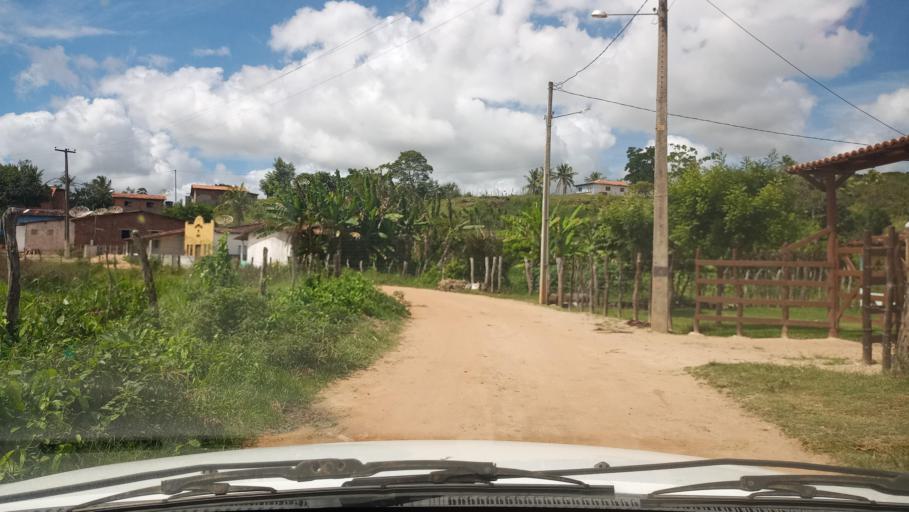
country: BR
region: Rio Grande do Norte
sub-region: Goianinha
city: Goianinha
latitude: -6.2621
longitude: -35.2577
